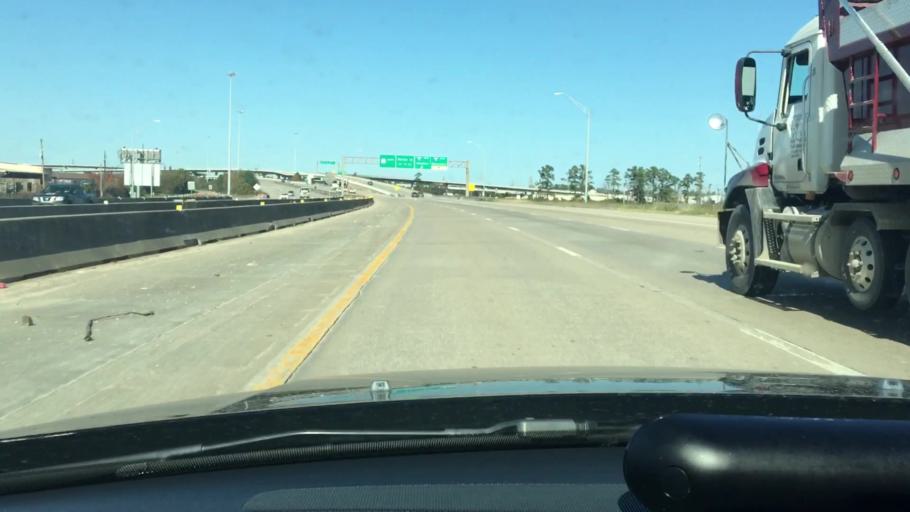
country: US
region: Texas
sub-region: Harris County
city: Cloverleaf
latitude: 29.7632
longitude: -95.1472
